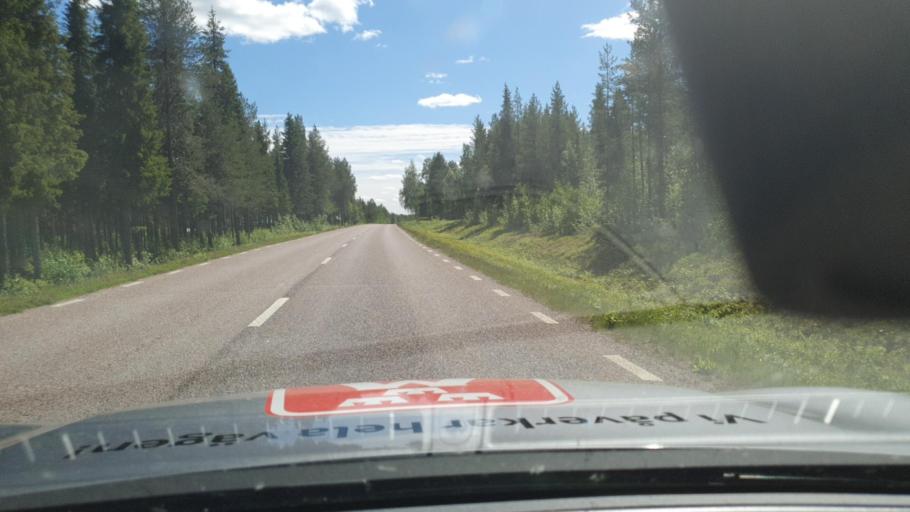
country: FI
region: Lapland
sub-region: Tunturi-Lappi
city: Kolari
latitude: 67.0594
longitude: 23.6740
